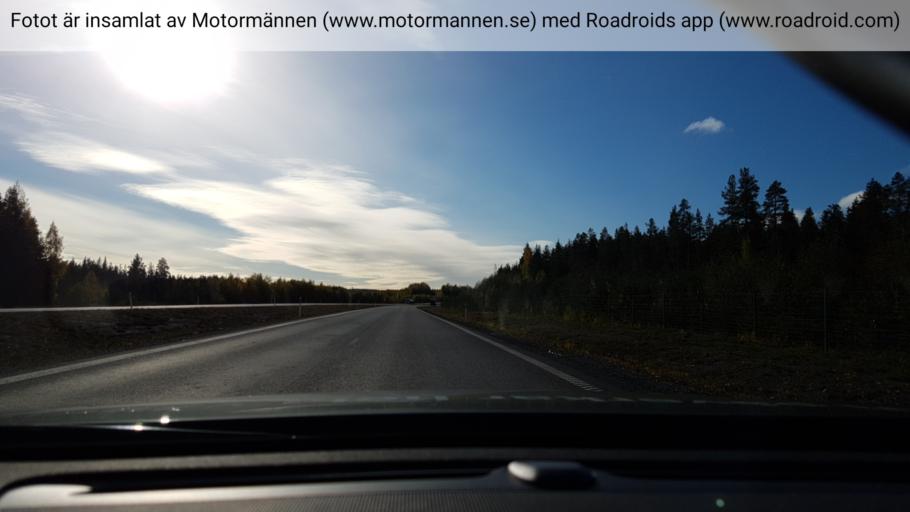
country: SE
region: Vaesterbotten
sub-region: Skelleftea Kommun
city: Kage
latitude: 64.8149
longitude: 21.0288
